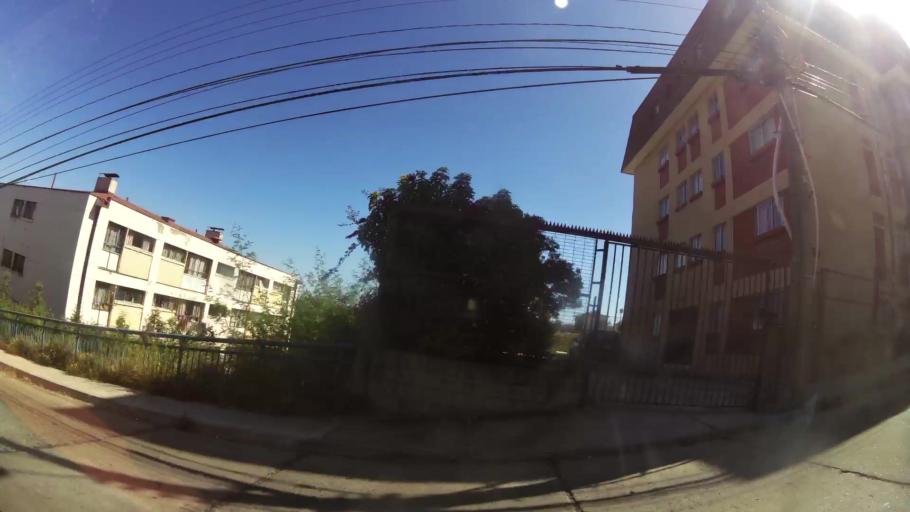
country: CL
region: Valparaiso
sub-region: Provincia de Valparaiso
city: Vina del Mar
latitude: -33.0584
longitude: -71.5827
